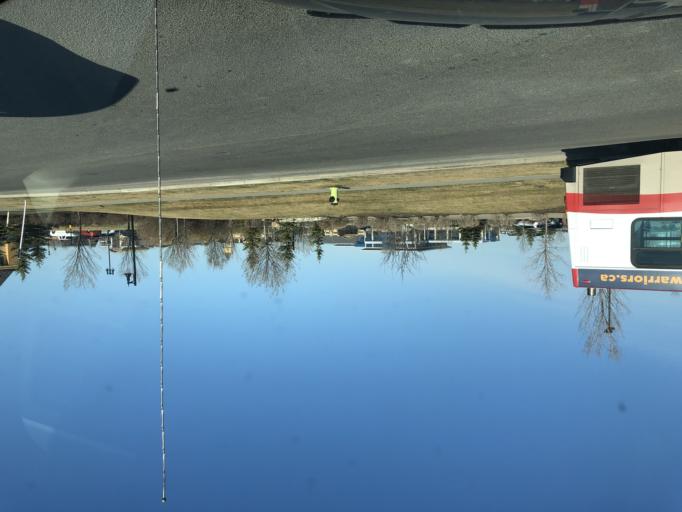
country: CA
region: Alberta
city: Calgary
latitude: 50.9608
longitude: -114.0072
